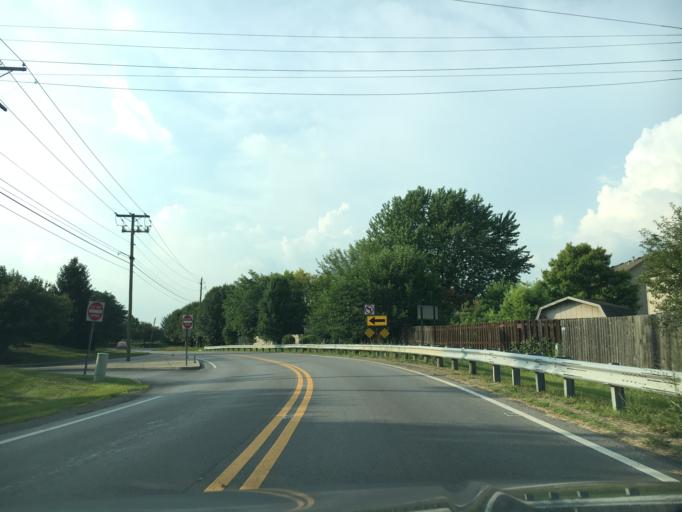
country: US
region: Ohio
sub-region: Franklin County
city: Hilliard
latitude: 39.9992
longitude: -83.1655
